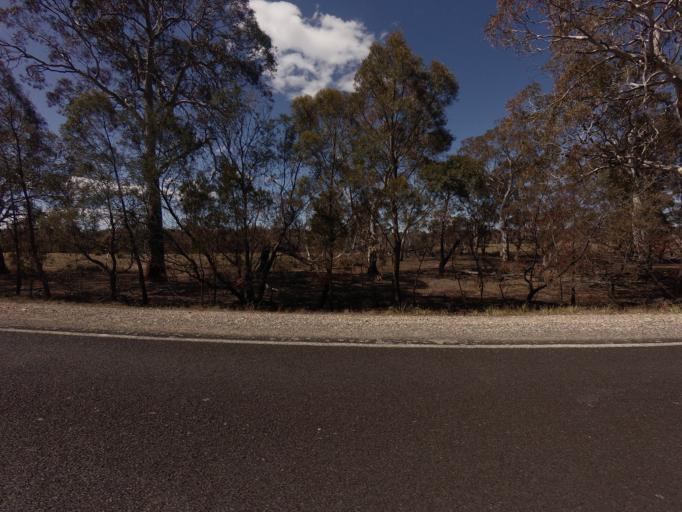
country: AU
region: Tasmania
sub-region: Break O'Day
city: St Helens
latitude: -42.0381
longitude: 148.0278
